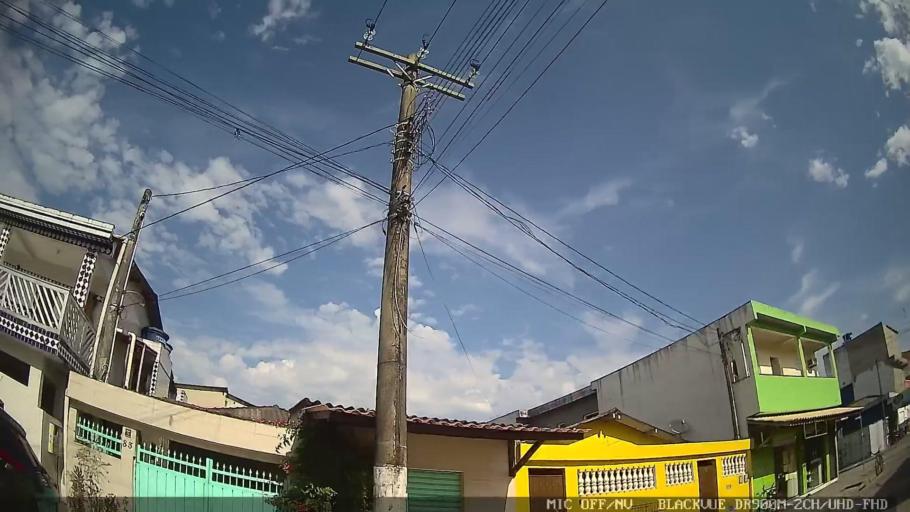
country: BR
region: Sao Paulo
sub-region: Guaruja
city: Guaruja
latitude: -23.9635
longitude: -46.2530
